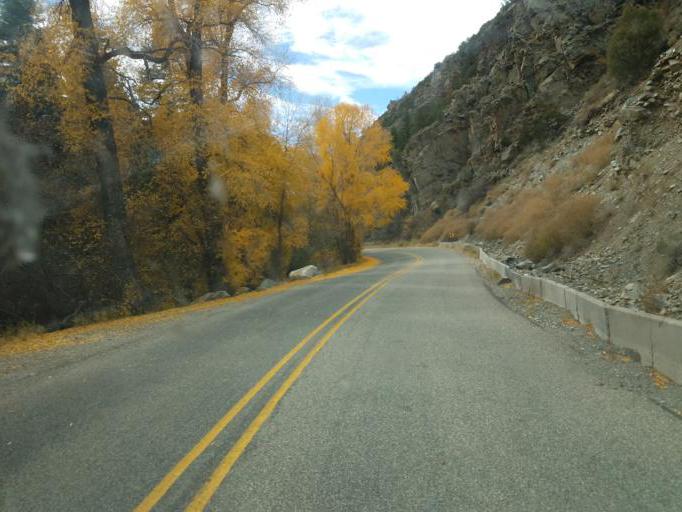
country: US
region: New Mexico
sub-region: Taos County
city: Arroyo Seco
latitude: 36.5449
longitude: -105.5534
